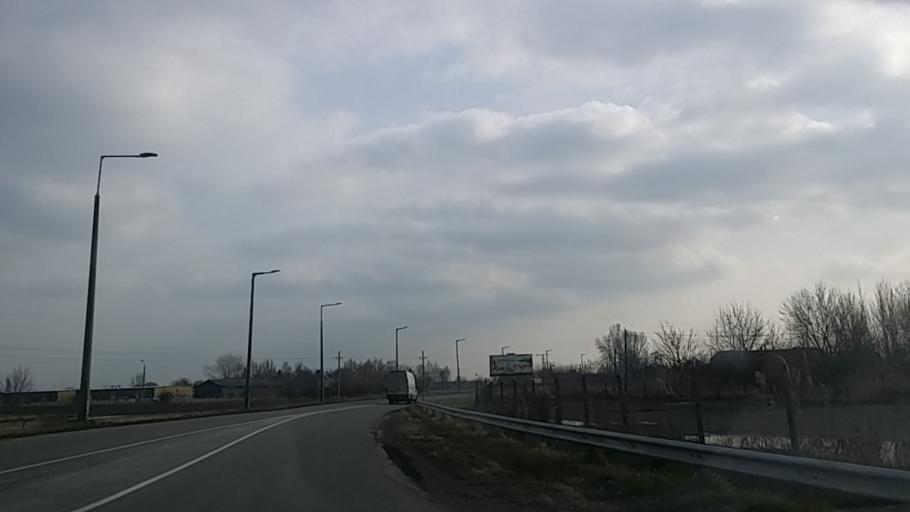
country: HU
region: Tolna
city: Szekszard
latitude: 46.3554
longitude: 18.7210
